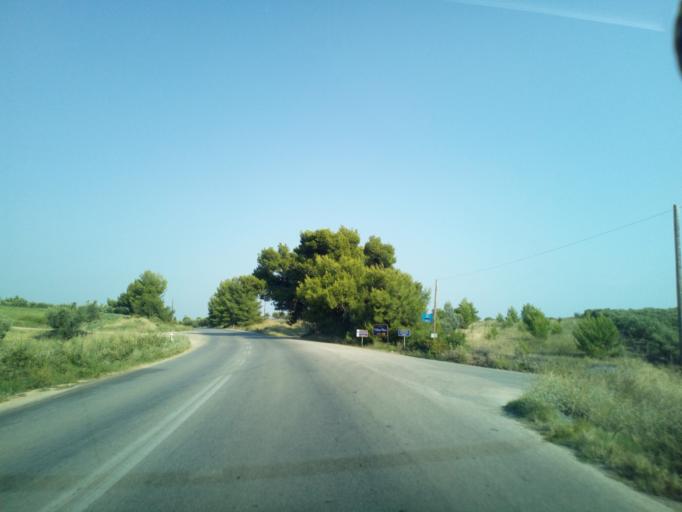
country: GR
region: Central Macedonia
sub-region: Nomos Chalkidikis
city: Ormylia
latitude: 40.2400
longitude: 23.5876
